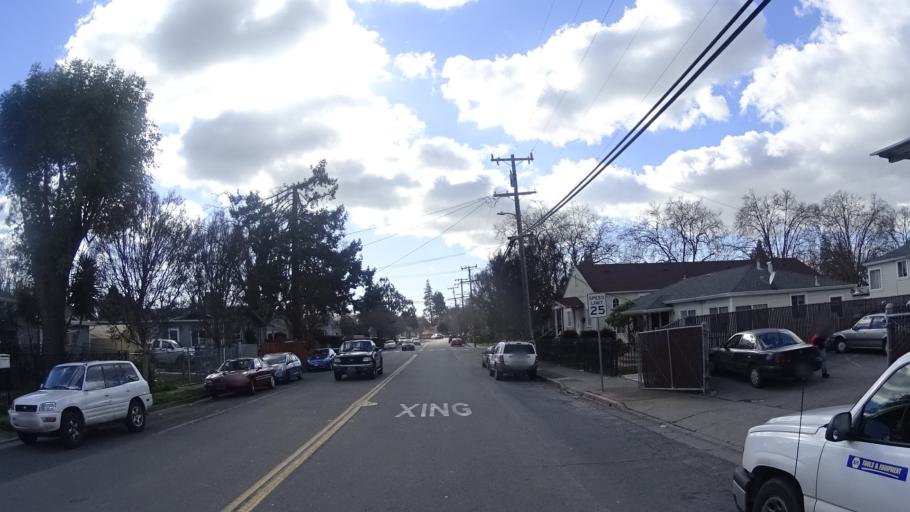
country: US
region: California
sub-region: Alameda County
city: Cherryland
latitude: 37.6816
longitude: -122.0962
